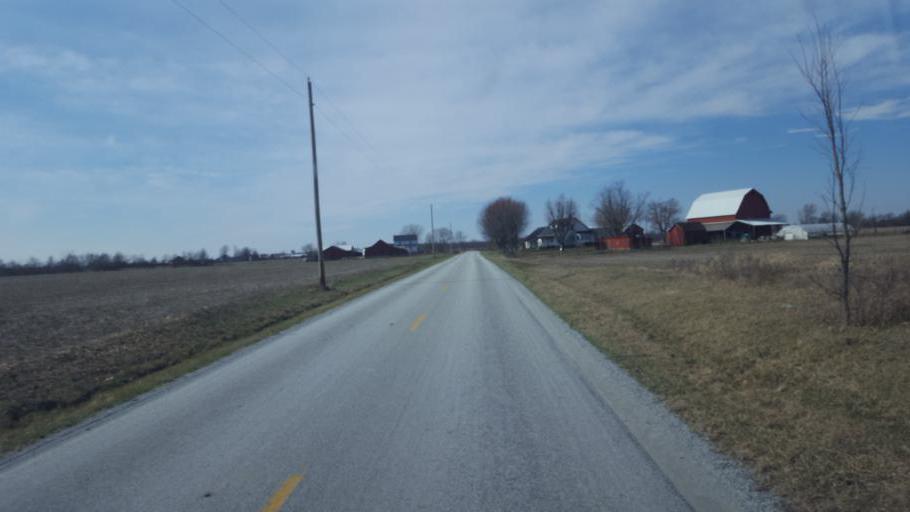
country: US
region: Ohio
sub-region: Hardin County
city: Kenton
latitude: 40.5736
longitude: -83.4348
